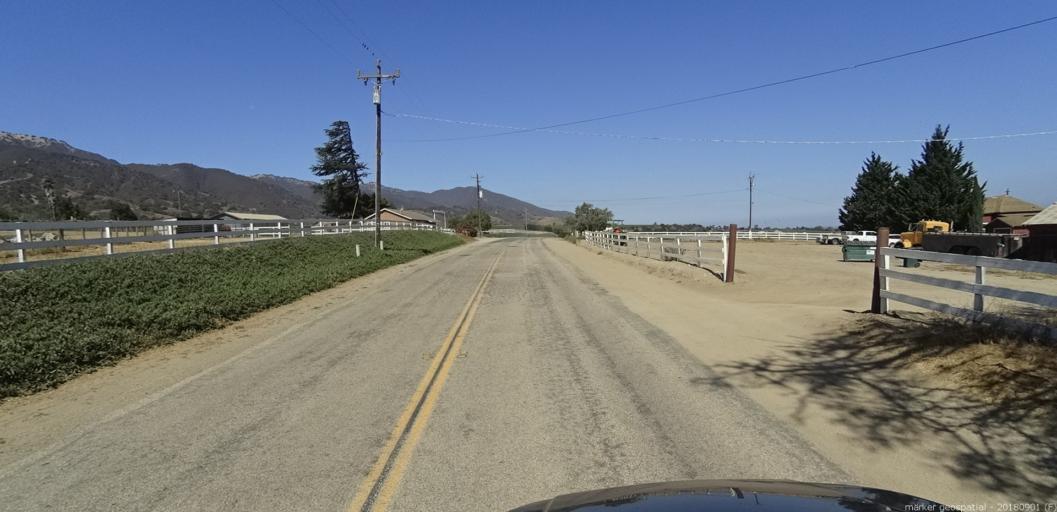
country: US
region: California
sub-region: Monterey County
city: Gonzales
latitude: 36.5051
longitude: -121.5092
